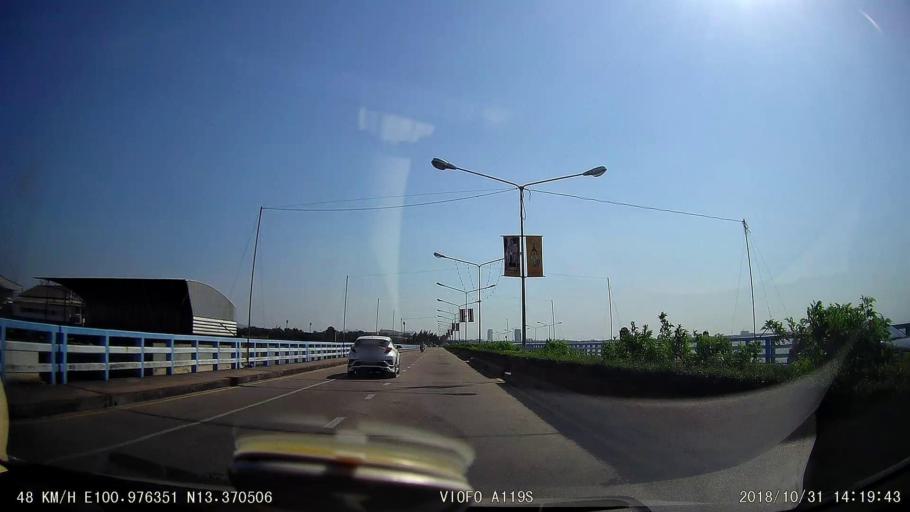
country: TH
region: Chon Buri
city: Chon Buri
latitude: 13.3696
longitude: 100.9763
